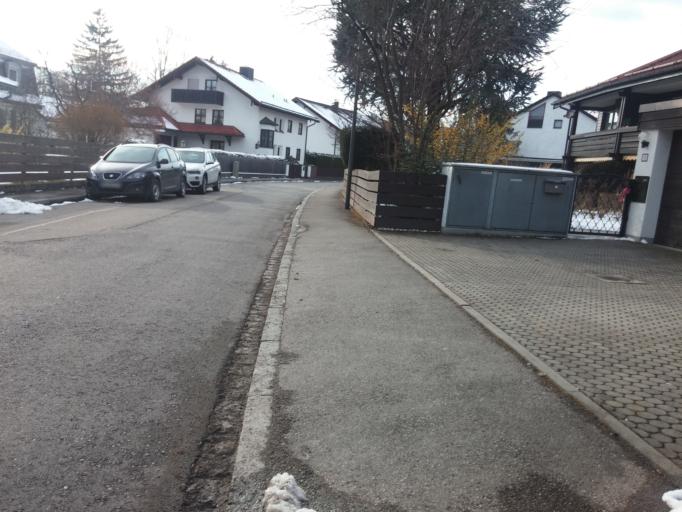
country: DE
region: Bavaria
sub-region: Upper Bavaria
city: Ottobrunn
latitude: 48.0729
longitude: 11.6662
